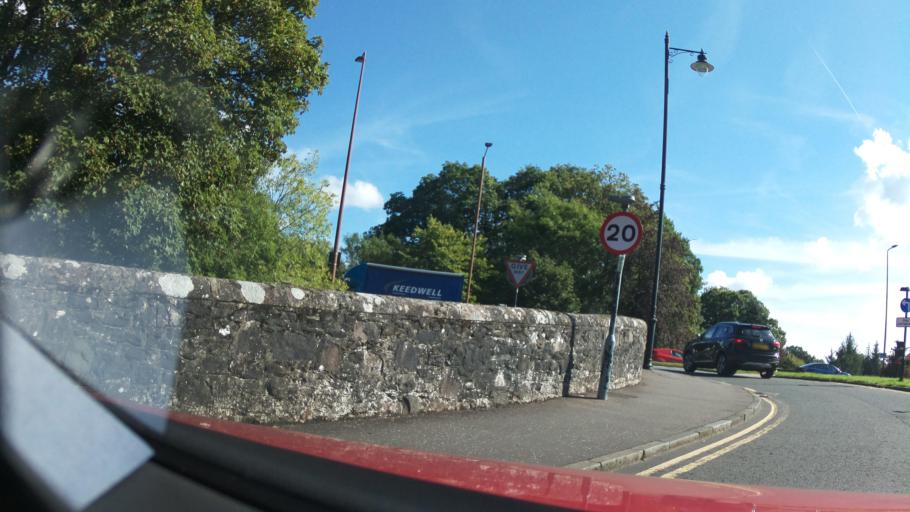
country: GB
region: Scotland
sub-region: Stirling
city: Dunblane
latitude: 56.1844
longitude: -3.9626
